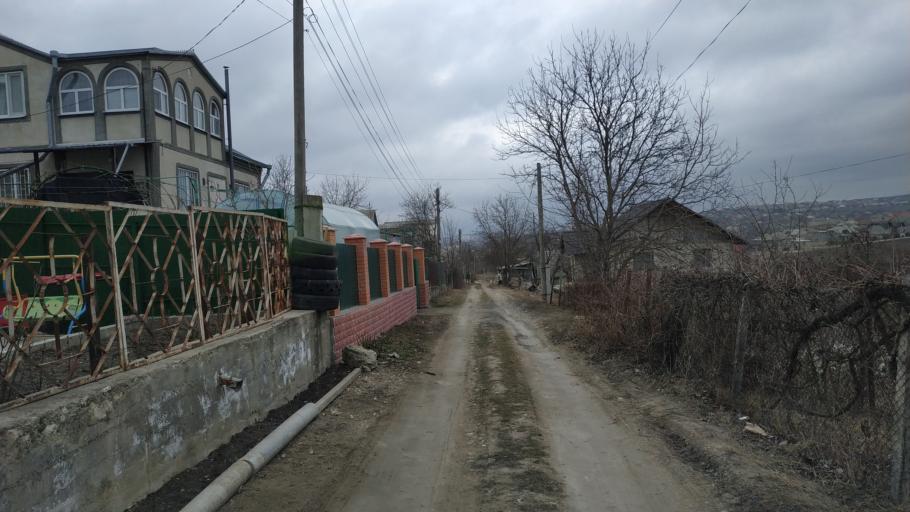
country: MD
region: Laloveni
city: Ialoveni
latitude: 46.9303
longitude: 28.7963
